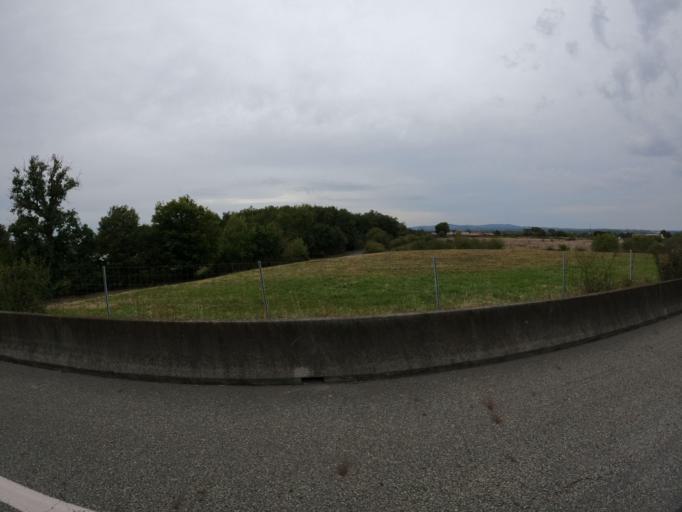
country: FR
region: Limousin
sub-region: Departement de la Creuse
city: Gouzon
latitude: 46.1942
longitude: 2.1777
